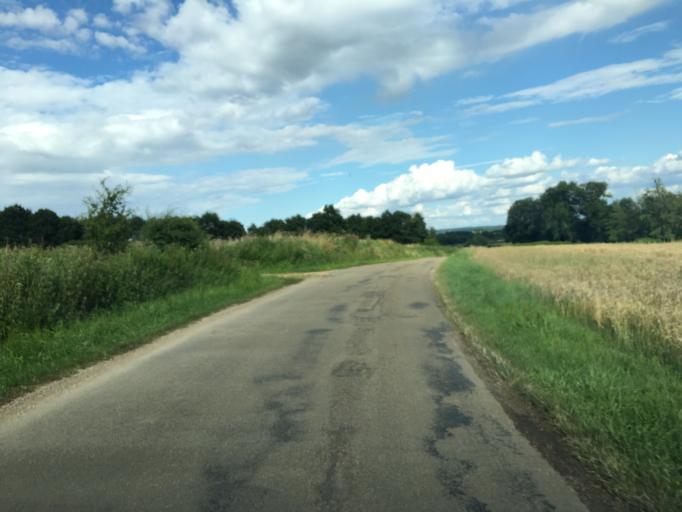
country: FR
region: Bourgogne
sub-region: Departement de l'Yonne
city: Appoigny
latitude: 47.8835
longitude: 3.5138
